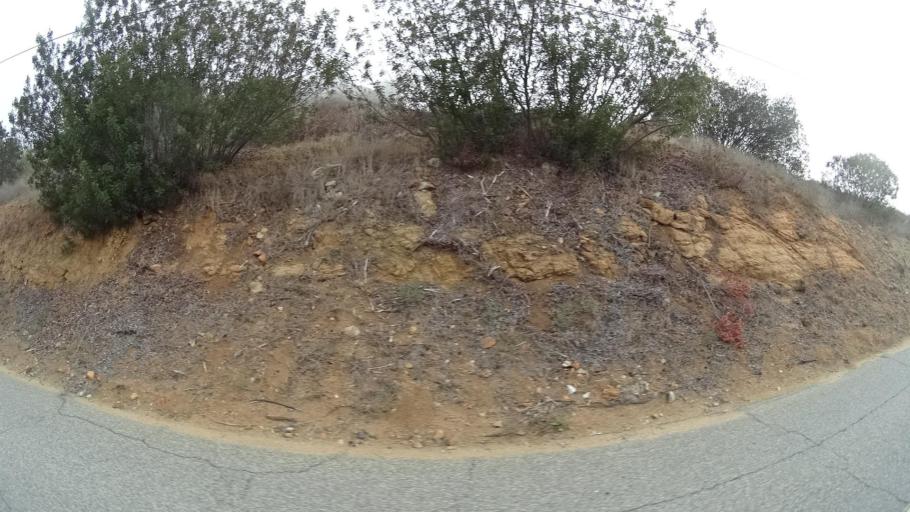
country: US
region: California
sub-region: San Diego County
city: Rainbow
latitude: 33.3472
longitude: -117.1758
